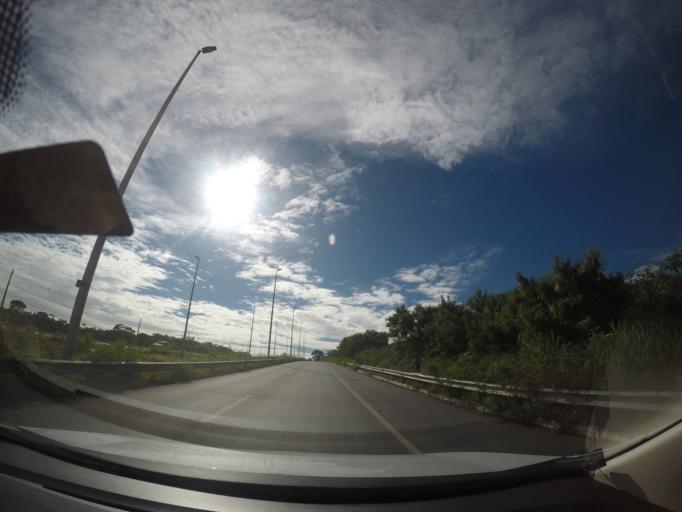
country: BR
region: Goias
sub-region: Goiania
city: Goiania
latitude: -16.6888
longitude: -49.1812
